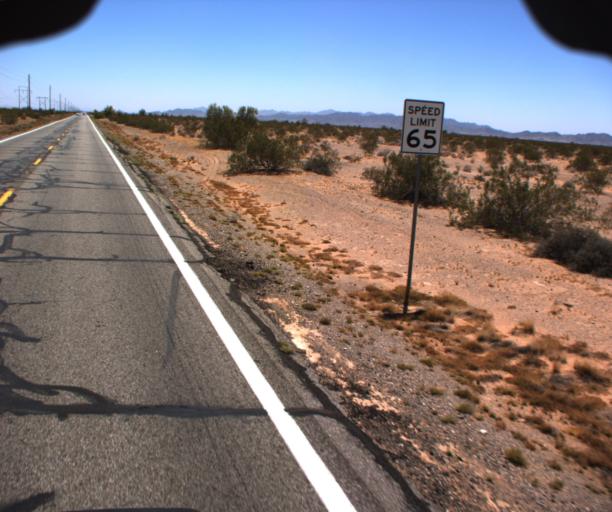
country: US
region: Arizona
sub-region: La Paz County
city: Quartzsite
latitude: 33.8432
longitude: -114.2170
